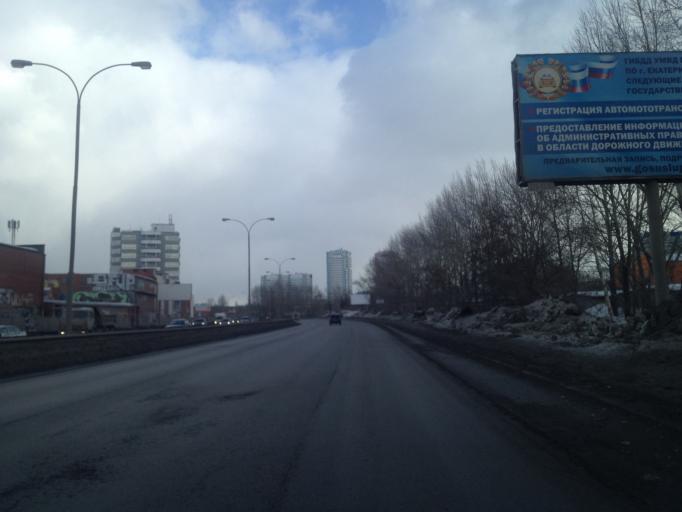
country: RU
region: Sverdlovsk
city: Yekaterinburg
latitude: 56.7875
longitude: 60.6255
